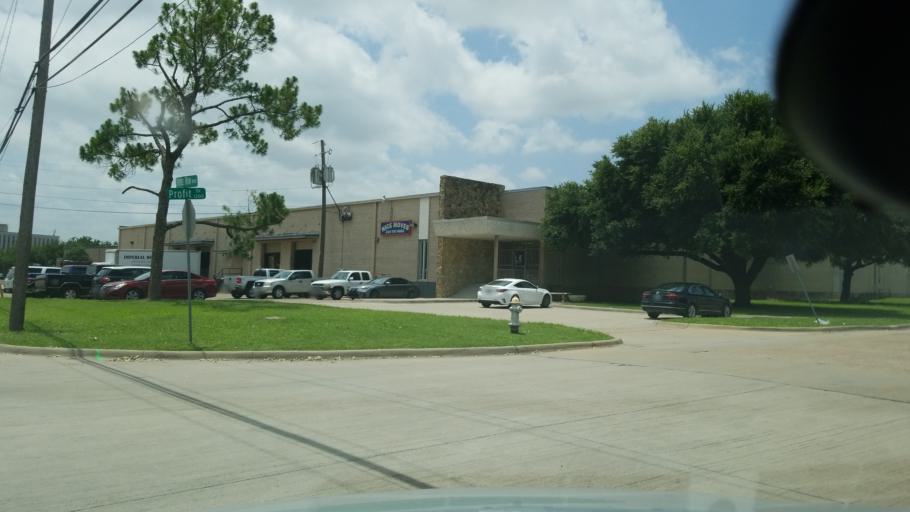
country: US
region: Texas
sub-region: Dallas County
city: Irving
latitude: 32.8290
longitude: -96.8762
